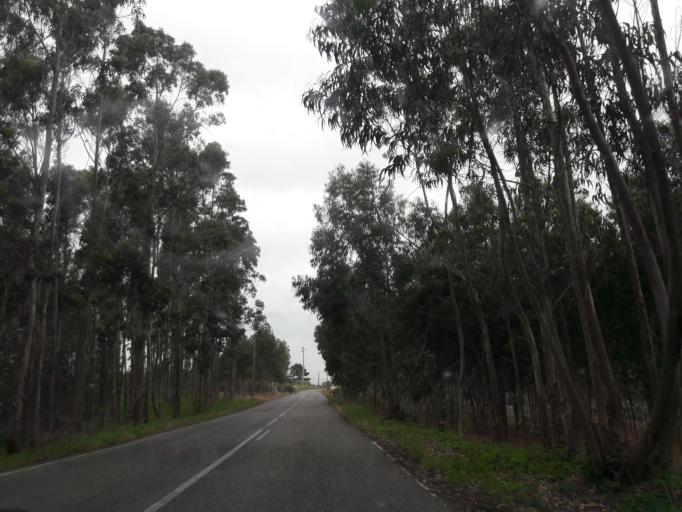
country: PT
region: Leiria
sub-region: Peniche
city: Atouguia da Baleia
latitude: 39.3459
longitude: -9.2832
